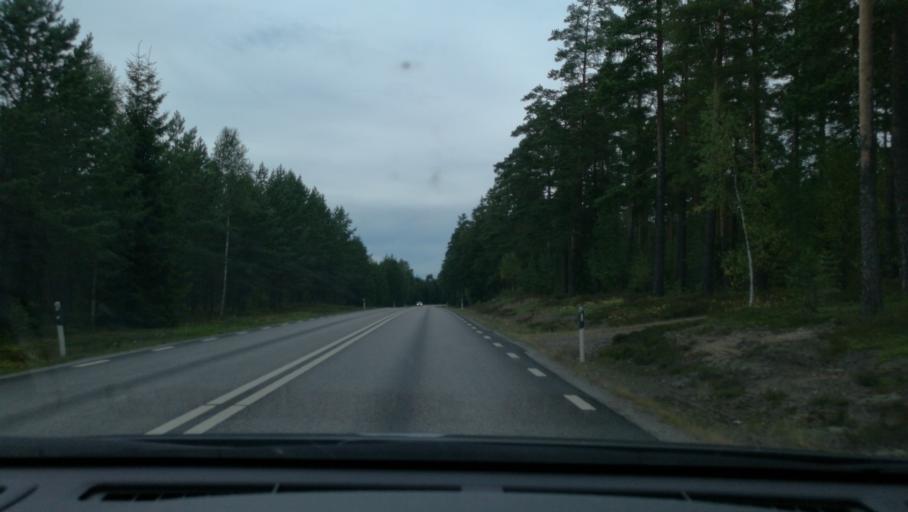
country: SE
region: Soedermanland
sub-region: Katrineholms Kommun
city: Katrineholm
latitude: 59.1211
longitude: 16.1575
